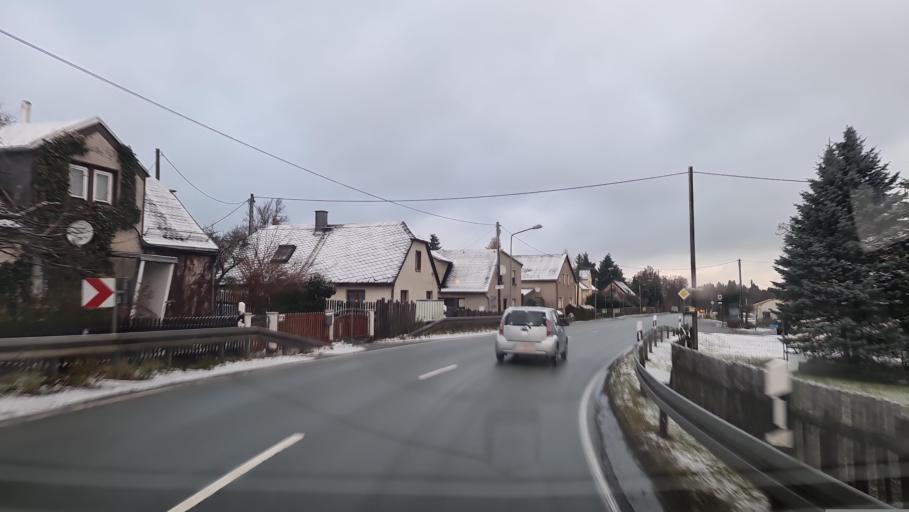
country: DE
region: Saxony
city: Limbach
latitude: 50.5828
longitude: 12.2745
